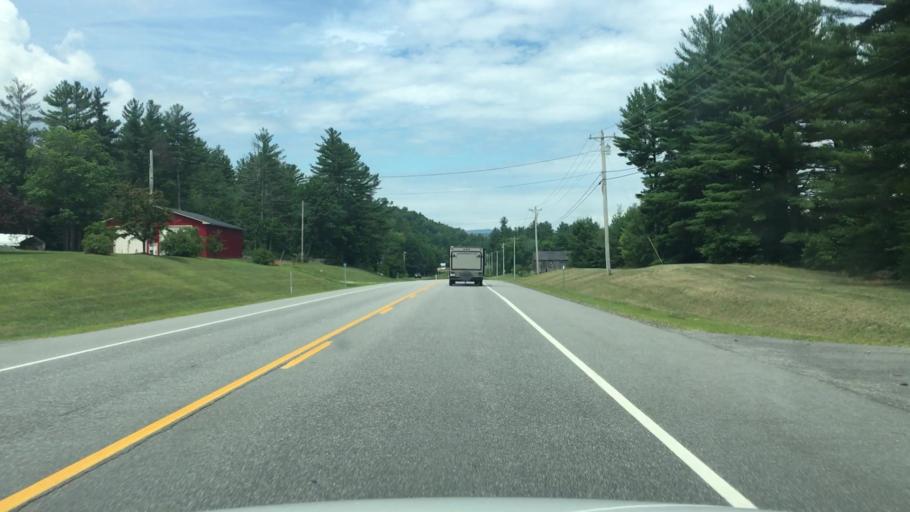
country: US
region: New Hampshire
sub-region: Grafton County
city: Rumney
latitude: 43.8302
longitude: -71.8962
